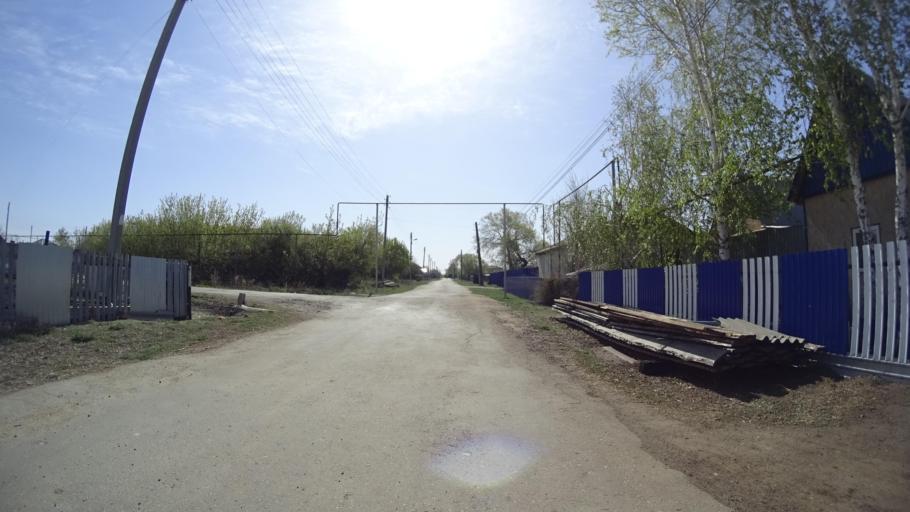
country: RU
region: Chelyabinsk
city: Chesma
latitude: 53.7945
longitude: 61.0308
